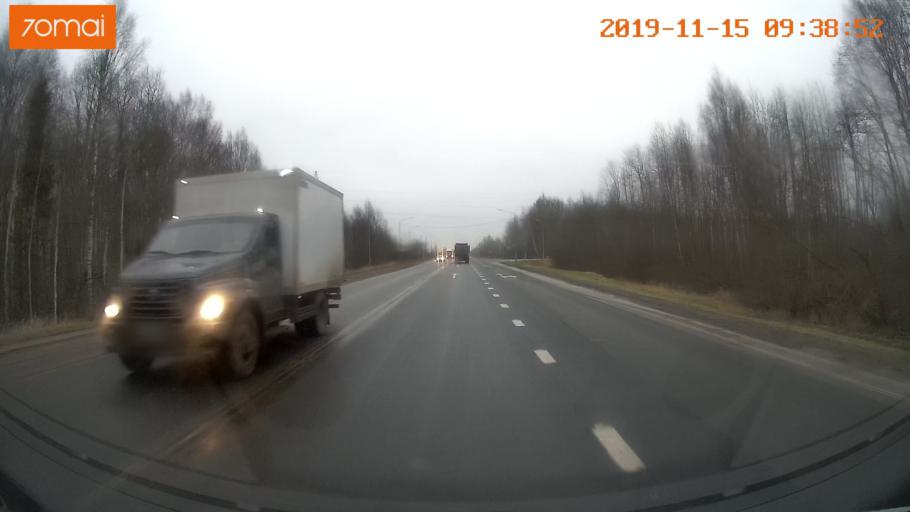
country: RU
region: Vologda
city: Sheksna
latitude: 59.2285
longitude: 38.4633
